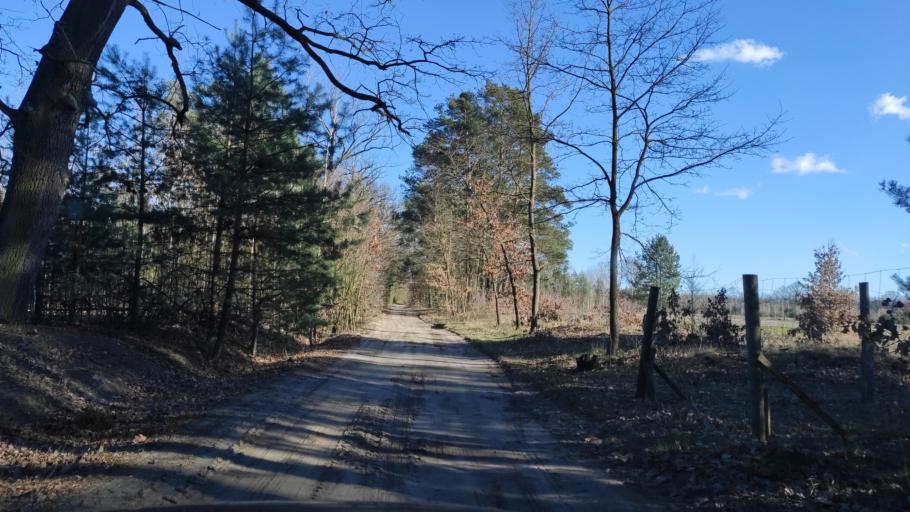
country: PL
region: Masovian Voivodeship
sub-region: Powiat radomski
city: Jastrzebia
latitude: 51.4542
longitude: 21.2769
